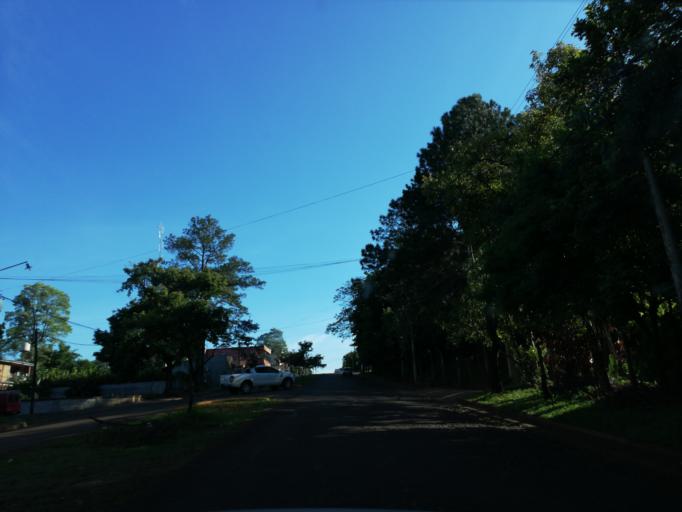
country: AR
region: Misiones
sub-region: Departamento de Obera
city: Obera
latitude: -27.4960
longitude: -55.1166
